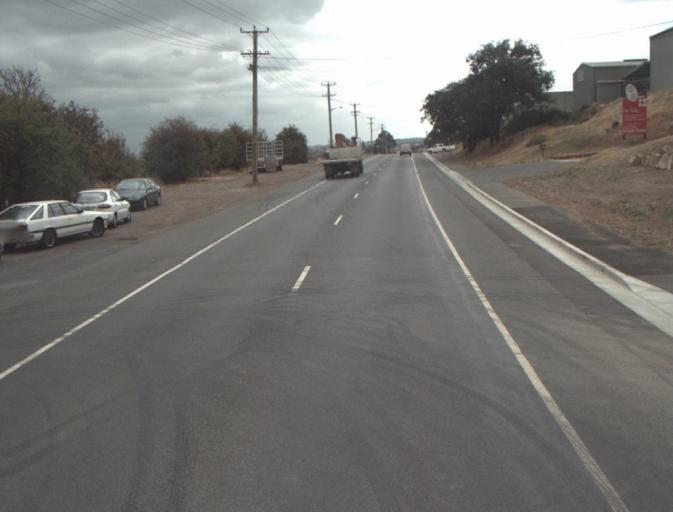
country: AU
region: Tasmania
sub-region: Launceston
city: Newstead
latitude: -41.4437
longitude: 147.1825
